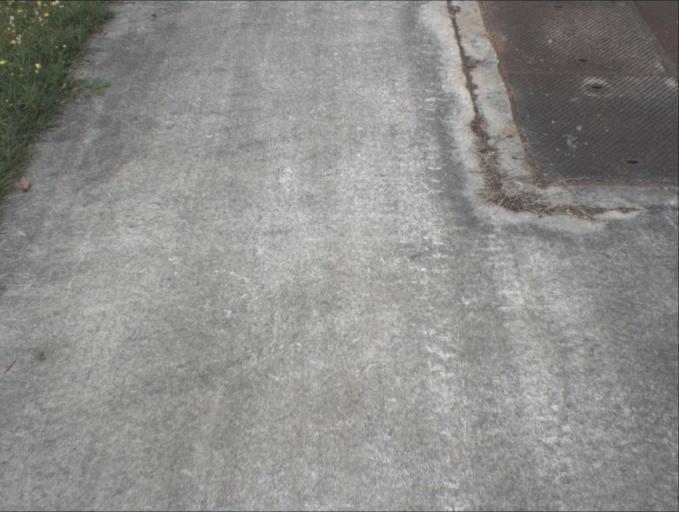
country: AU
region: Queensland
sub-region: Logan
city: Logan Reserve
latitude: -27.7055
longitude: 153.0758
